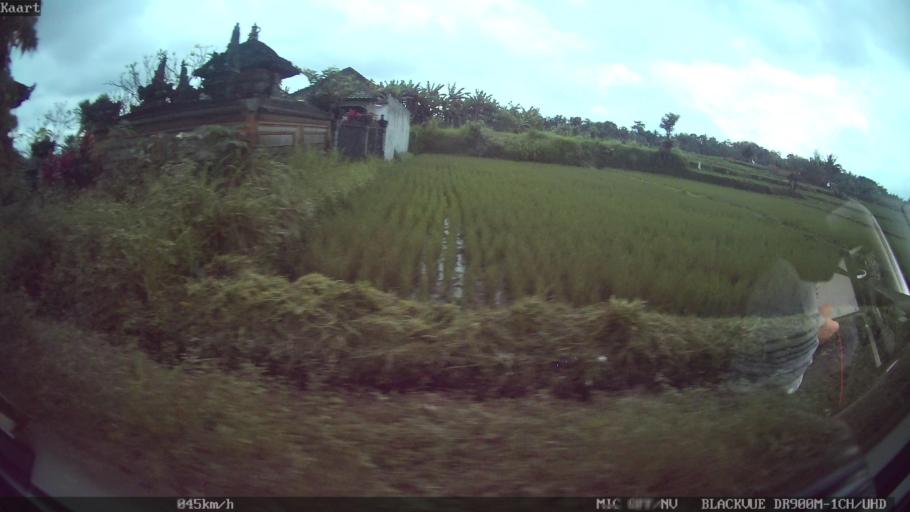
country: ID
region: Bali
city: Banjar Teguan
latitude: -8.5023
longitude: 115.2253
